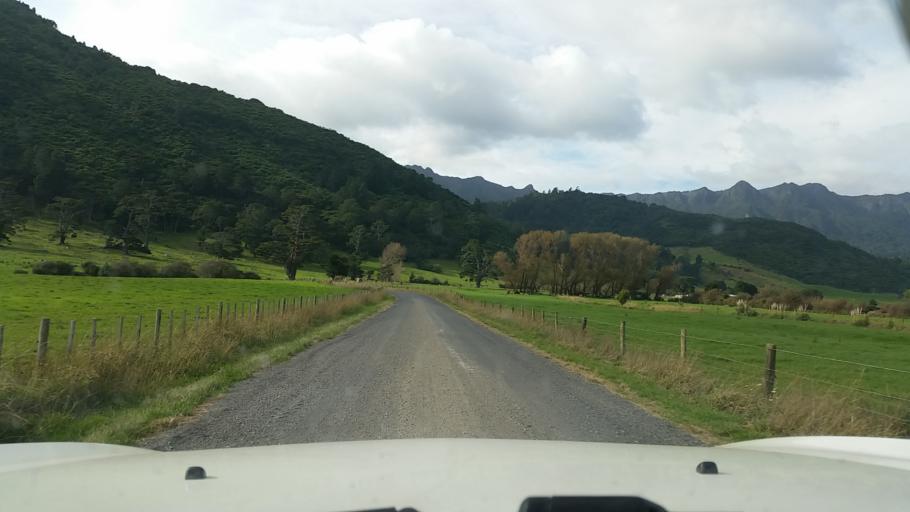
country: NZ
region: Bay of Plenty
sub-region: Western Bay of Plenty District
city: Katikati
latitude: -37.5635
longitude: 175.7426
